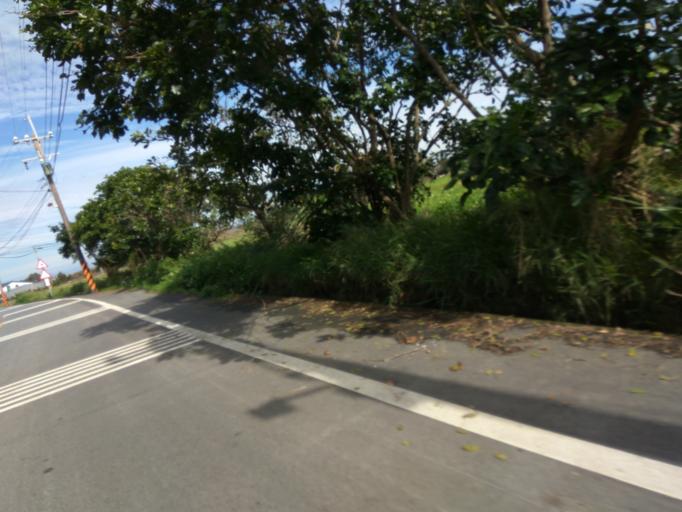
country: TW
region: Taiwan
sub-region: Hsinchu
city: Zhubei
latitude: 25.0005
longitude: 121.0875
